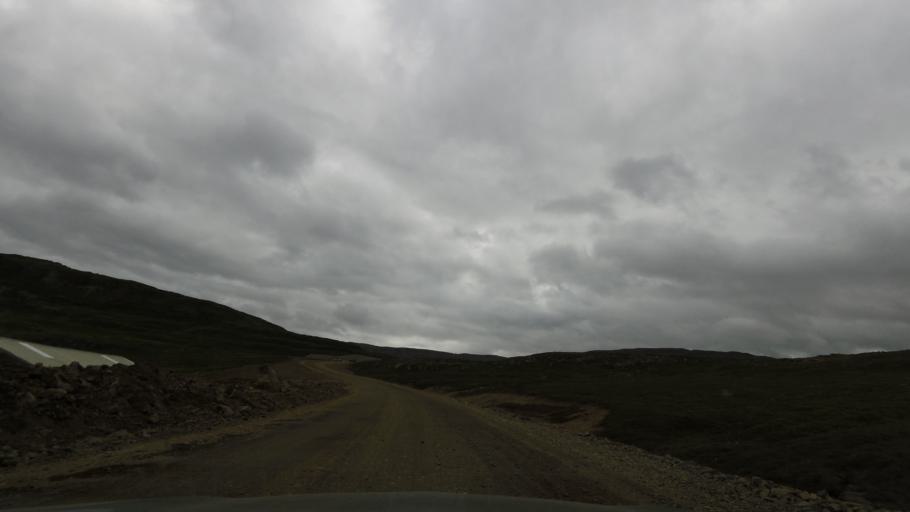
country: IS
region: Westfjords
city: Isafjoerdur
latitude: 65.9670
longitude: -22.9193
